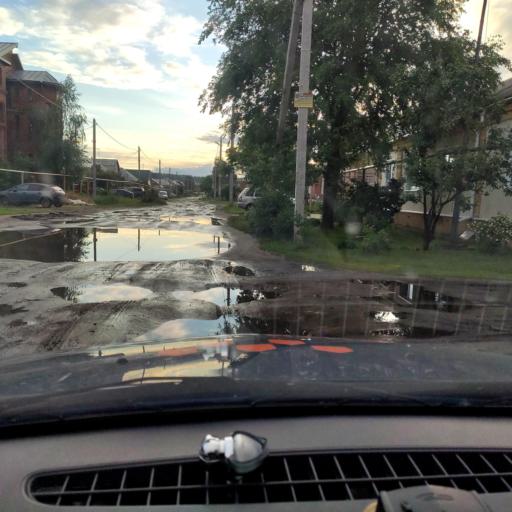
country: RU
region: Voronezj
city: Somovo
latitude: 51.7514
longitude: 39.3315
